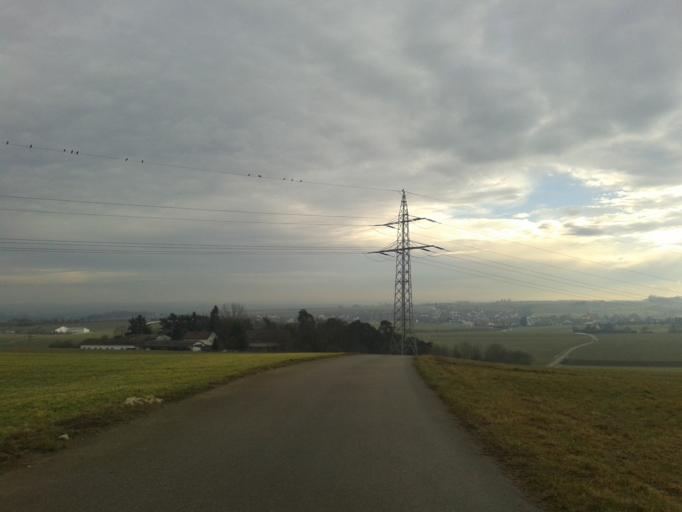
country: DE
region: Baden-Wuerttemberg
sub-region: Tuebingen Region
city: Erbach
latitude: 48.3676
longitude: 9.8969
